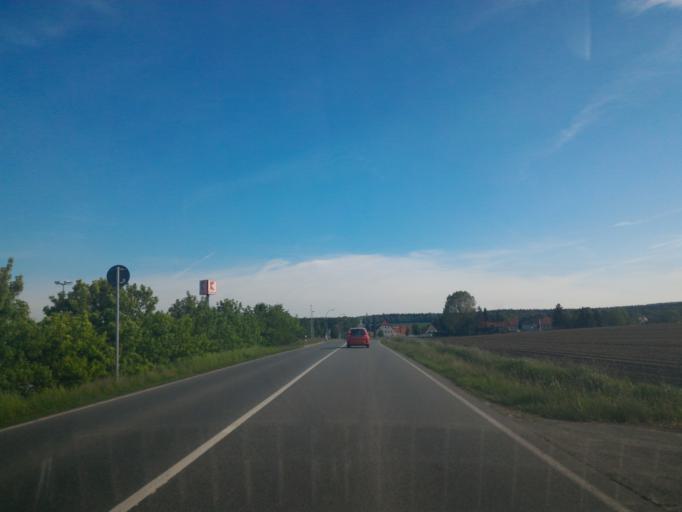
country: DE
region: Saxony
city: Neugersdorf
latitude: 50.9997
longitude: 14.6176
